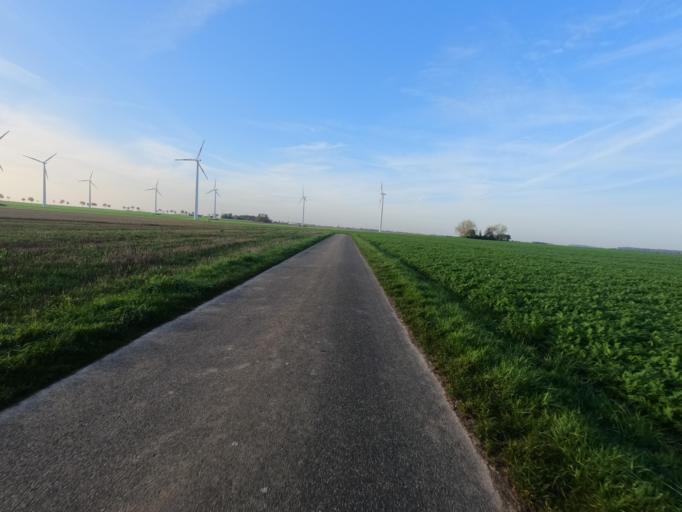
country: DE
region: North Rhine-Westphalia
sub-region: Regierungsbezirk Koln
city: Titz
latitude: 51.0533
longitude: 6.3803
